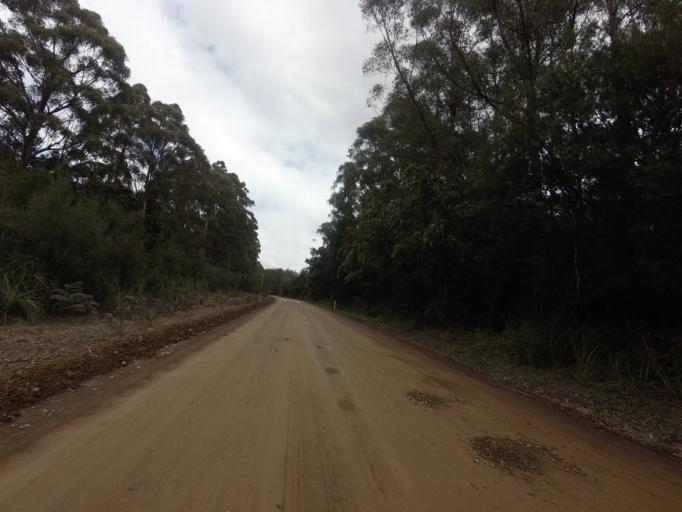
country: AU
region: Tasmania
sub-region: Huon Valley
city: Geeveston
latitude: -43.4132
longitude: 146.8969
